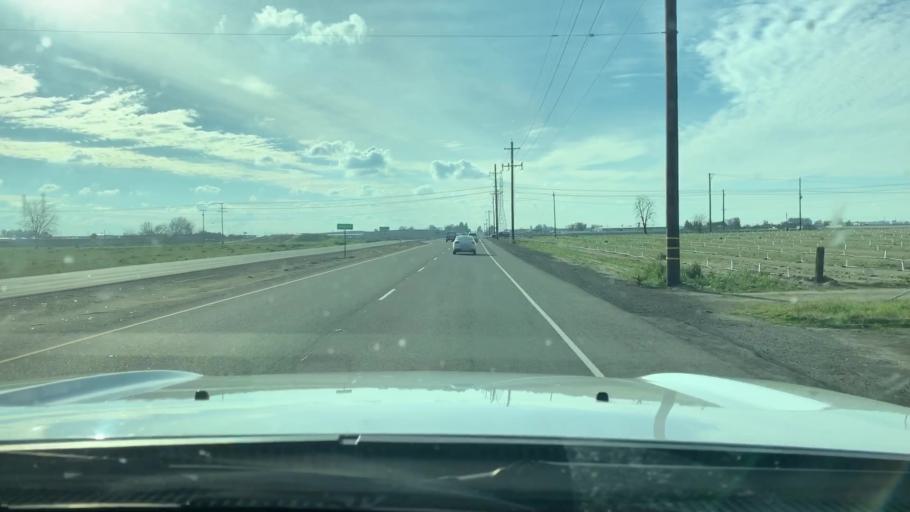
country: US
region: California
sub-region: Fresno County
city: Selma
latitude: 36.6057
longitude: -119.6350
